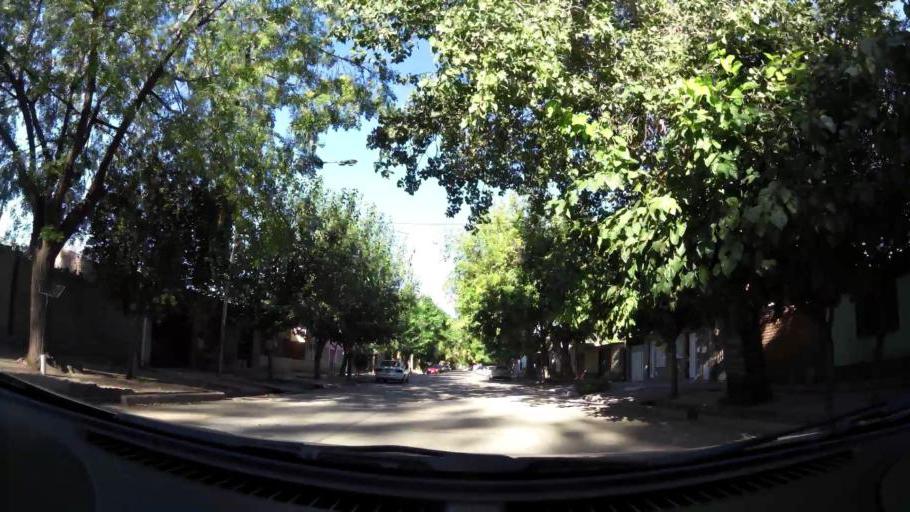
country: AR
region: Mendoza
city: Las Heras
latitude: -32.8430
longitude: -68.8267
